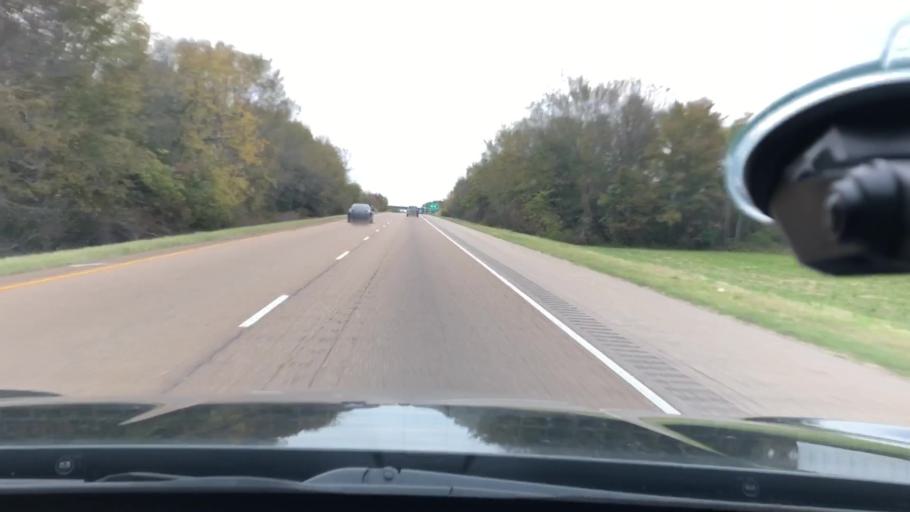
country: US
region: Arkansas
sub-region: Nevada County
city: Prescott
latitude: 33.8062
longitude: -93.4291
